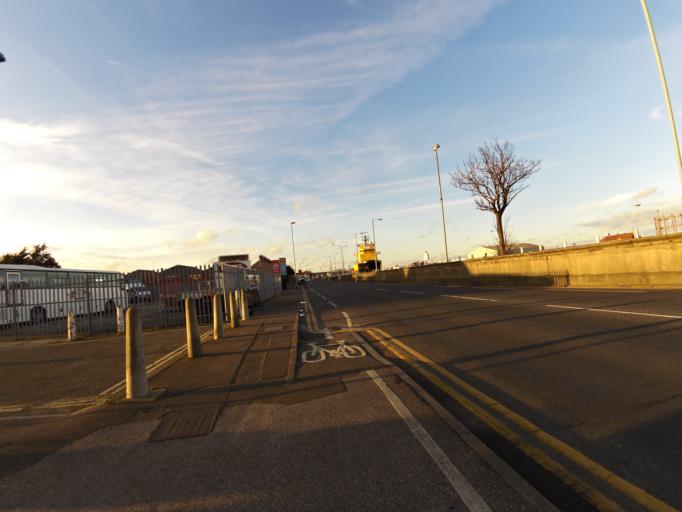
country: GB
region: England
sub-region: Norfolk
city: Great Yarmouth
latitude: 52.5918
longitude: 1.7252
